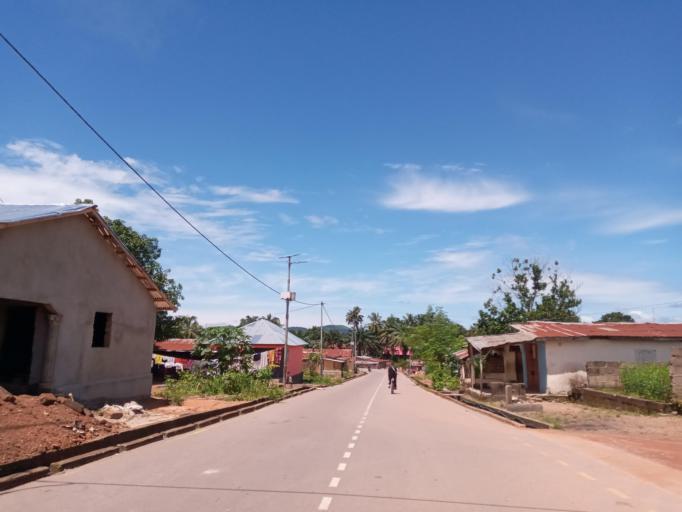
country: SL
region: Eastern Province
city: Koidu
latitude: 8.6470
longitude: -10.9636
